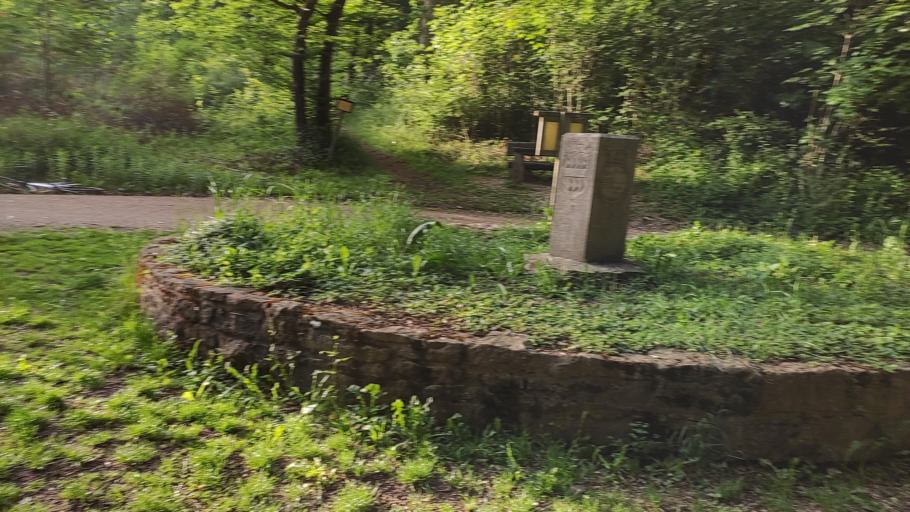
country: DE
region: Baden-Wuerttemberg
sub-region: Freiburg Region
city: Bollschweil
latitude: 47.9358
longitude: 7.7810
